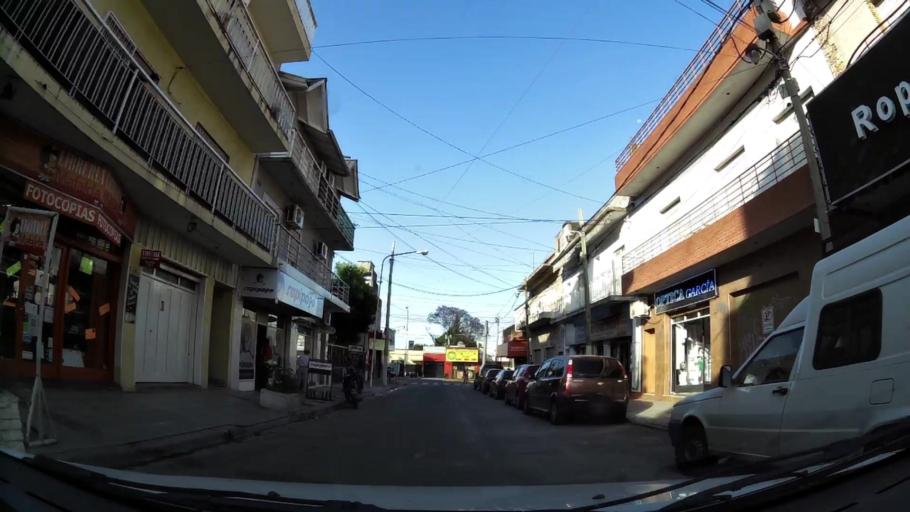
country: AR
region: Buenos Aires
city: Caseros
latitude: -34.5868
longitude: -58.5886
